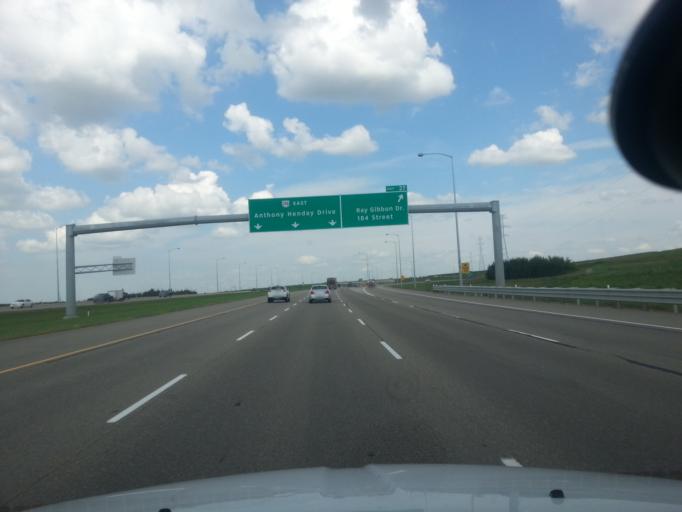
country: CA
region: Alberta
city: St. Albert
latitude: 53.5850
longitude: -113.6545
